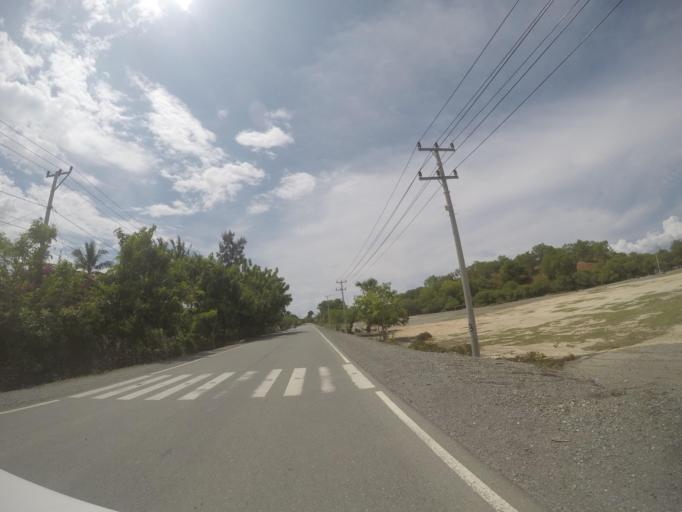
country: TL
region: Liquica
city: Liquica
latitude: -8.5652
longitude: 125.4193
